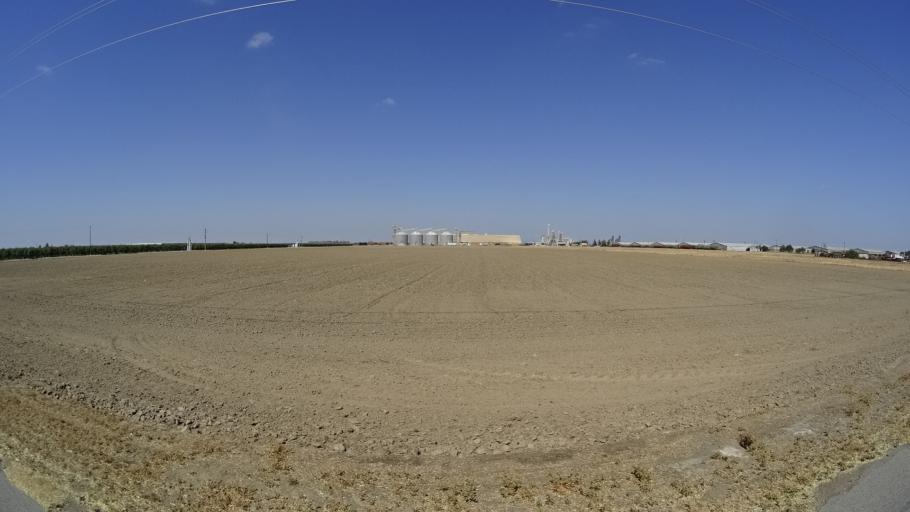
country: US
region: California
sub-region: Kings County
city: Home Garden
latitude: 36.2671
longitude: -119.6369
